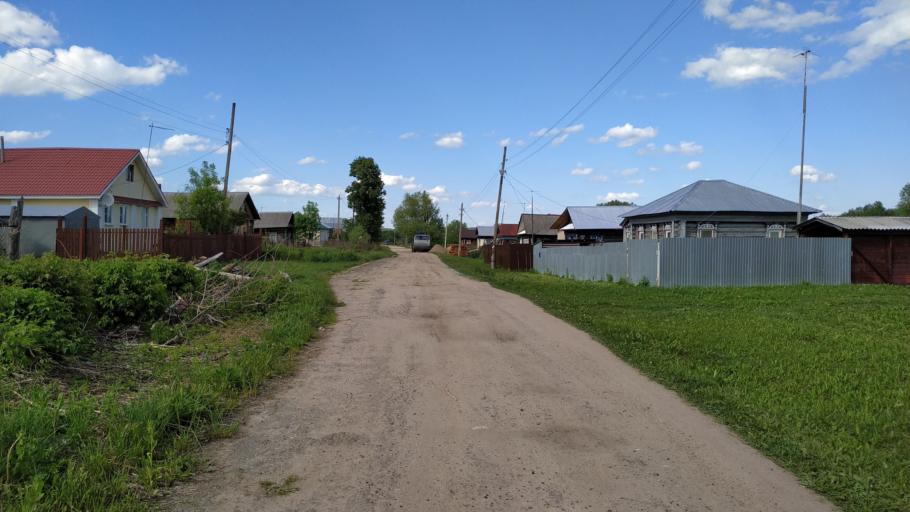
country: RU
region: Nizjnij Novgorod
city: Bogorodsk
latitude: 55.8854
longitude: 43.5574
